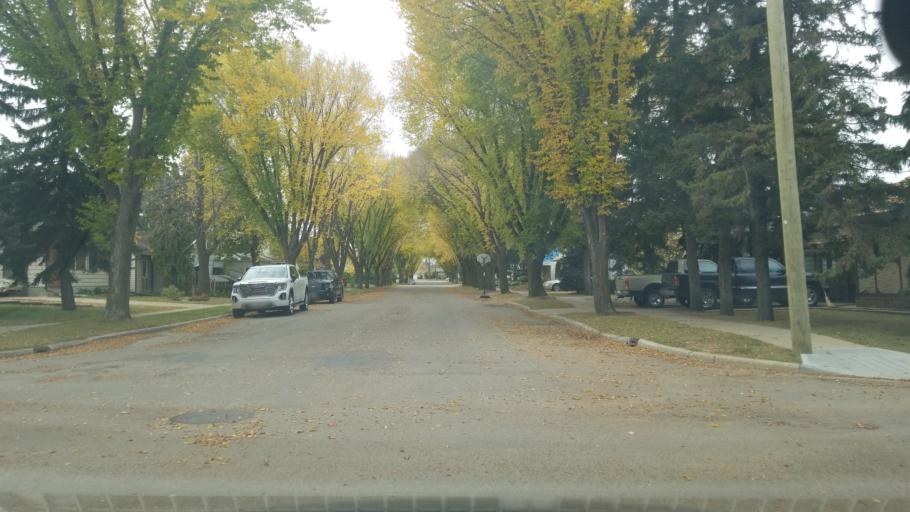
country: CA
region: Saskatchewan
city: Lloydminster
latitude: 53.2798
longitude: -110.0155
